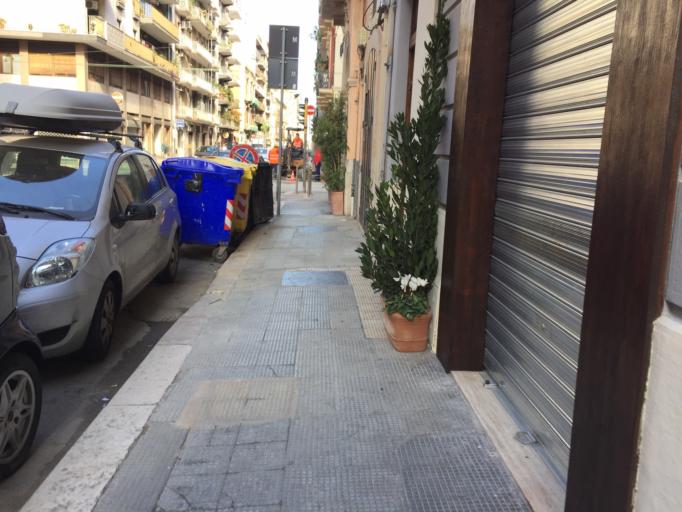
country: IT
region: Apulia
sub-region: Provincia di Bari
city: Bari
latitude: 41.1220
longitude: 16.8644
